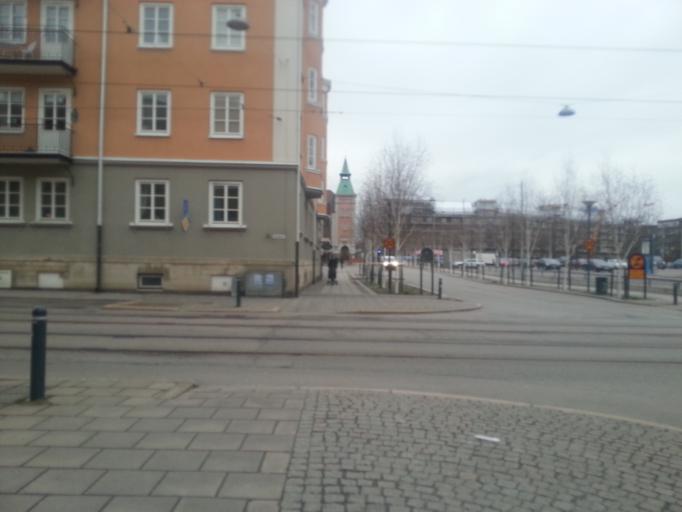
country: SE
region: OEstergoetland
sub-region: Norrkopings Kommun
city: Norrkoping
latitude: 58.5854
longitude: 16.1924
